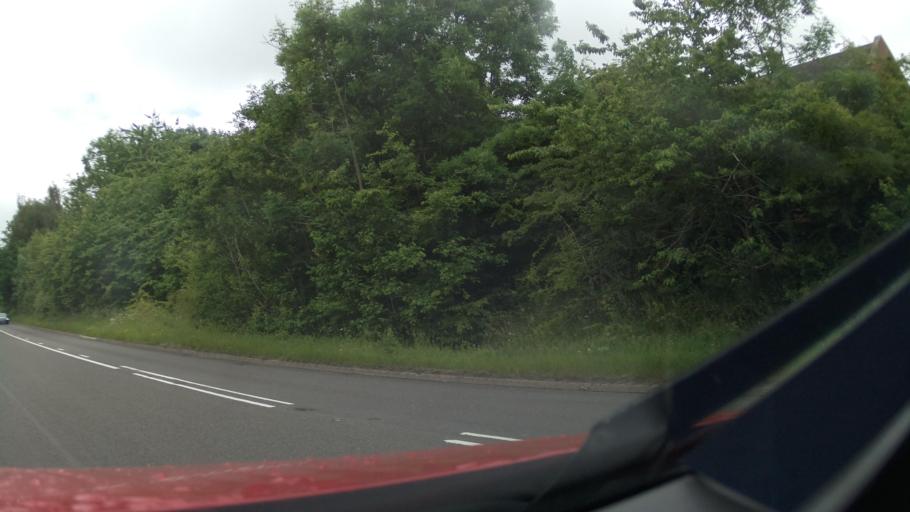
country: GB
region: England
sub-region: Staffordshire
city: Burton upon Trent
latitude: 52.8566
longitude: -1.6791
